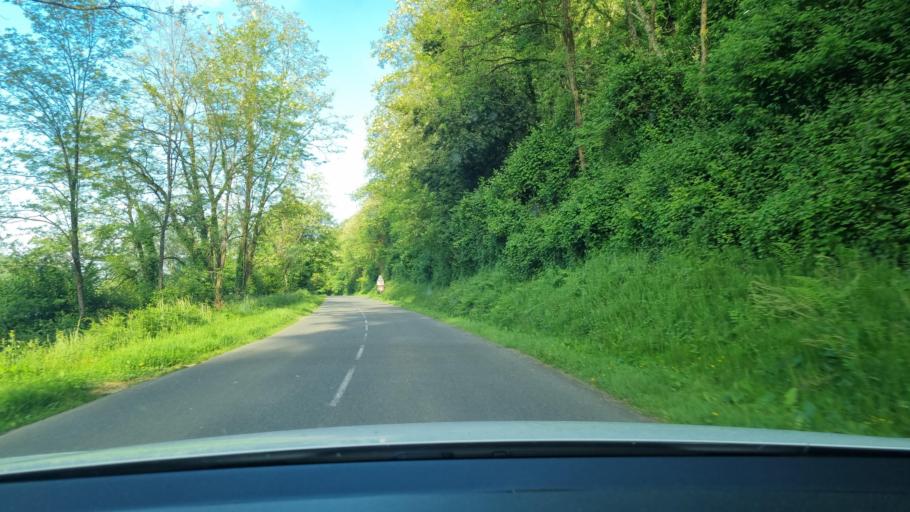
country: FR
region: Aquitaine
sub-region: Departement des Landes
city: Peyrehorade
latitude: 43.5359
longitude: -1.1535
